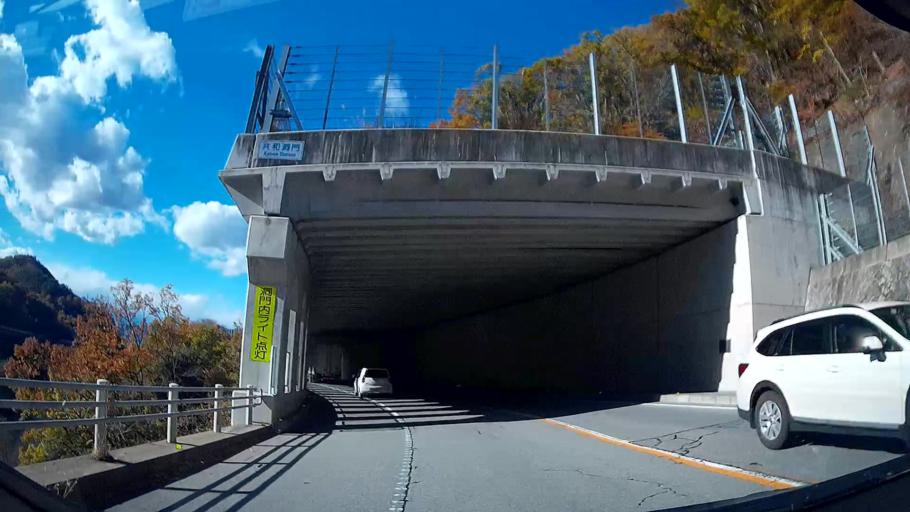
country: JP
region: Yamanashi
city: Enzan
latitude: 35.6512
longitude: 138.7567
